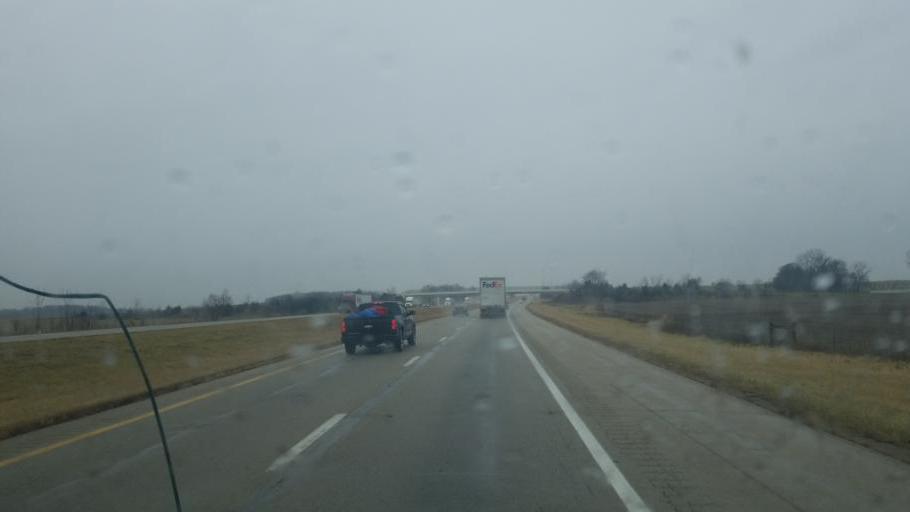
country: US
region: Ohio
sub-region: Preble County
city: New Paris
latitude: 39.8289
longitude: -84.7428
